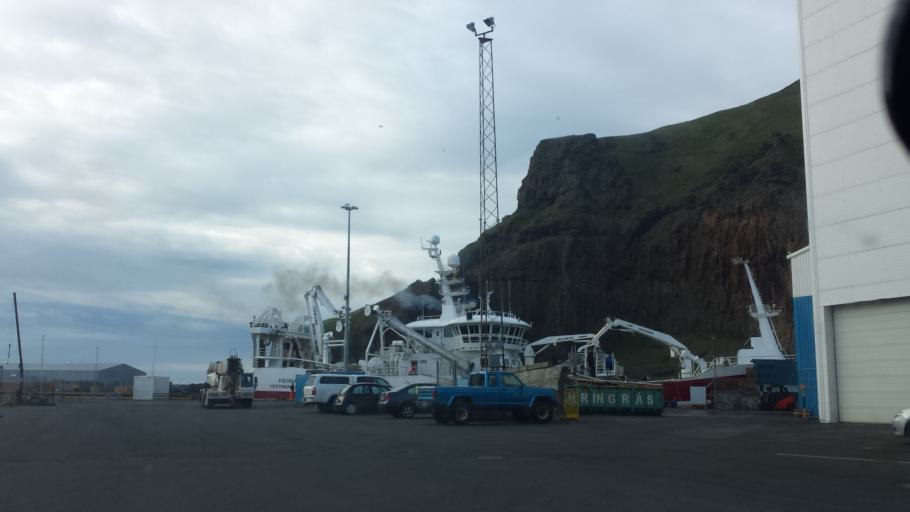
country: IS
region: South
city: Vestmannaeyjar
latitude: 63.4435
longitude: -20.2669
